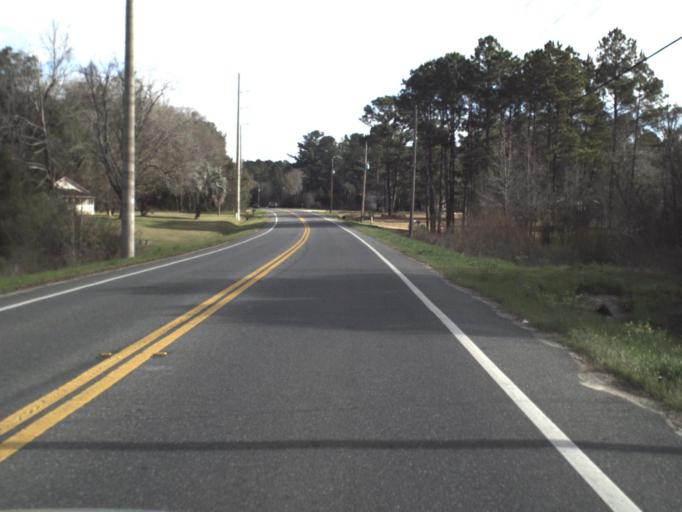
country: US
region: Florida
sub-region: Jackson County
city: Marianna
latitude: 30.7853
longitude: -85.1875
